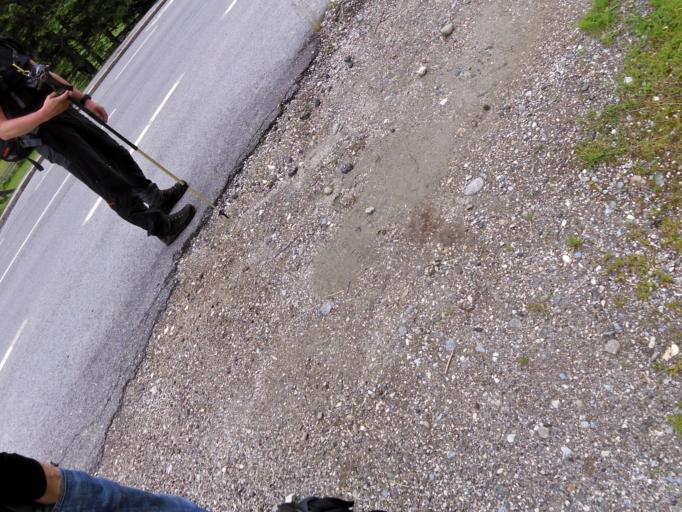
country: AT
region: Tyrol
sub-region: Politischer Bezirk Innsbruck Land
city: Neustift im Stubaital
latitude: 47.0471
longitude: 11.2315
